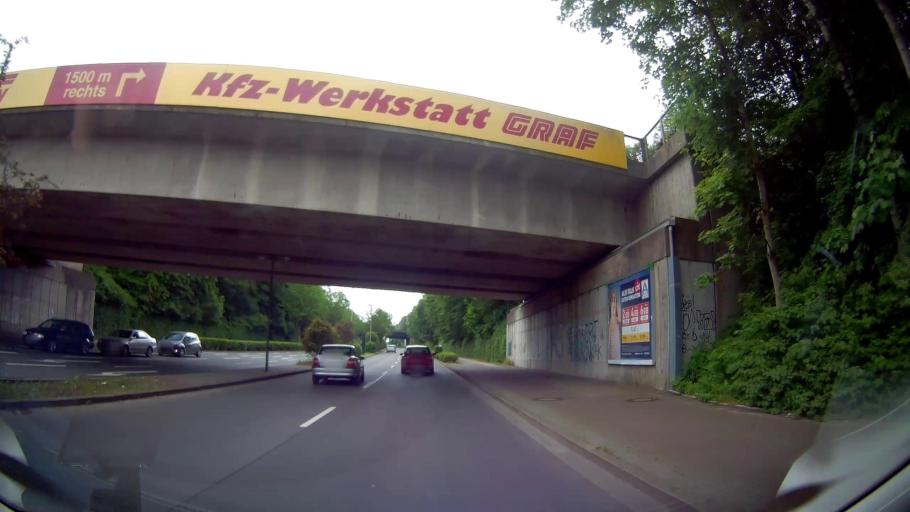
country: DE
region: North Rhine-Westphalia
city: Bochum-Hordel
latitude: 51.5240
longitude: 7.1550
